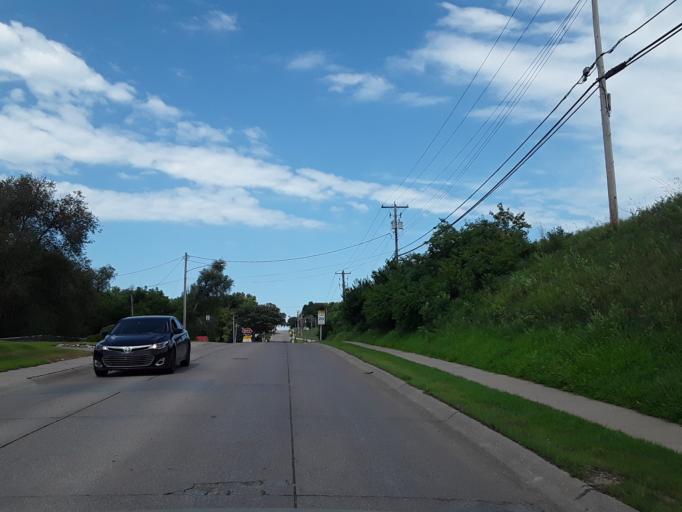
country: US
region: Nebraska
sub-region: Cass County
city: Plattsmouth
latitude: 41.0026
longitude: -95.8965
